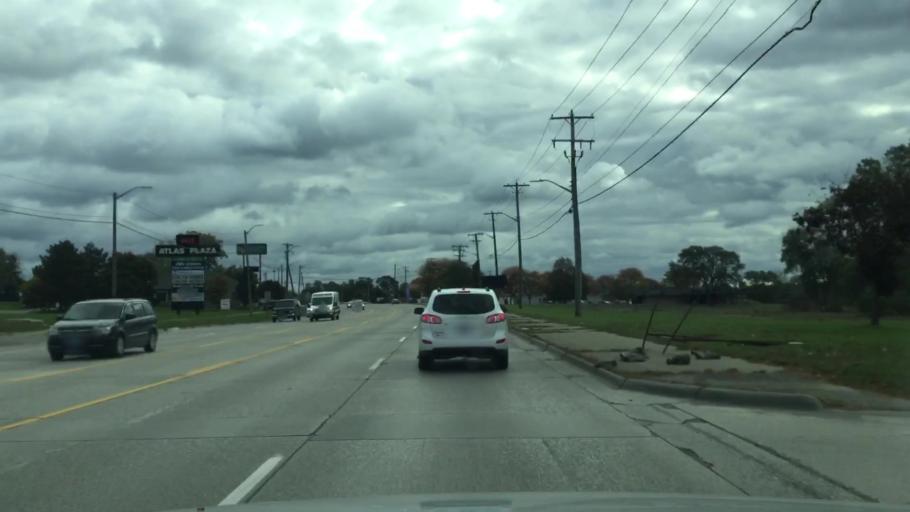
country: US
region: Michigan
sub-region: Oakland County
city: Waterford
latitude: 42.6599
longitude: -83.4292
